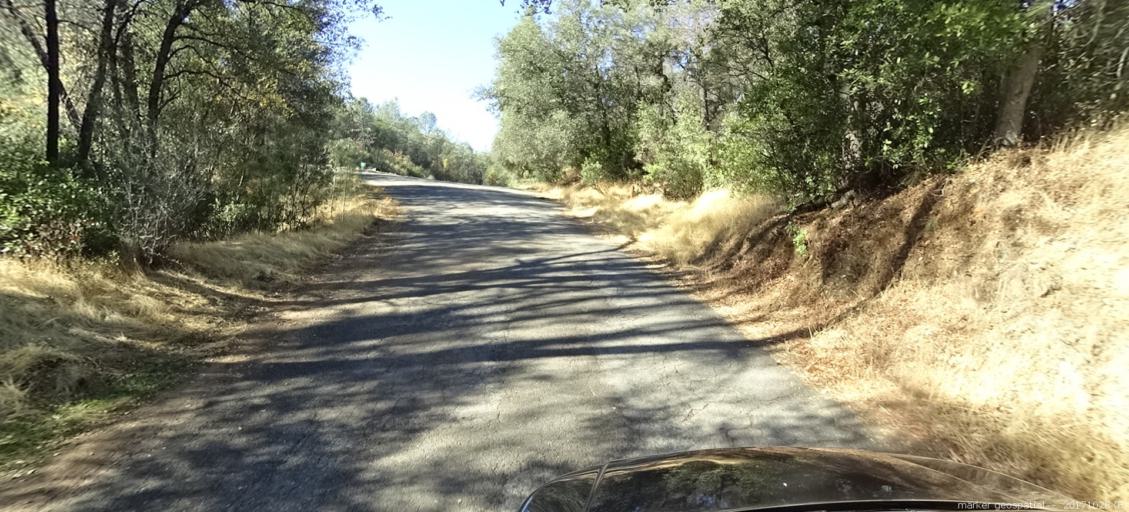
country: US
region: California
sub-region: Shasta County
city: Shasta
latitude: 40.5908
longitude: -122.4601
